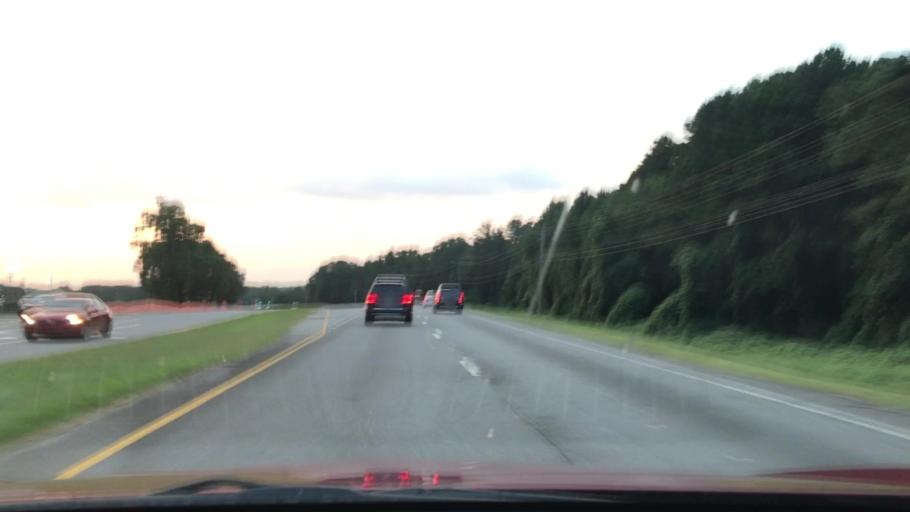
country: US
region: Georgia
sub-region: Gwinnett County
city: Lawrenceville
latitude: 34.0370
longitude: -83.9883
